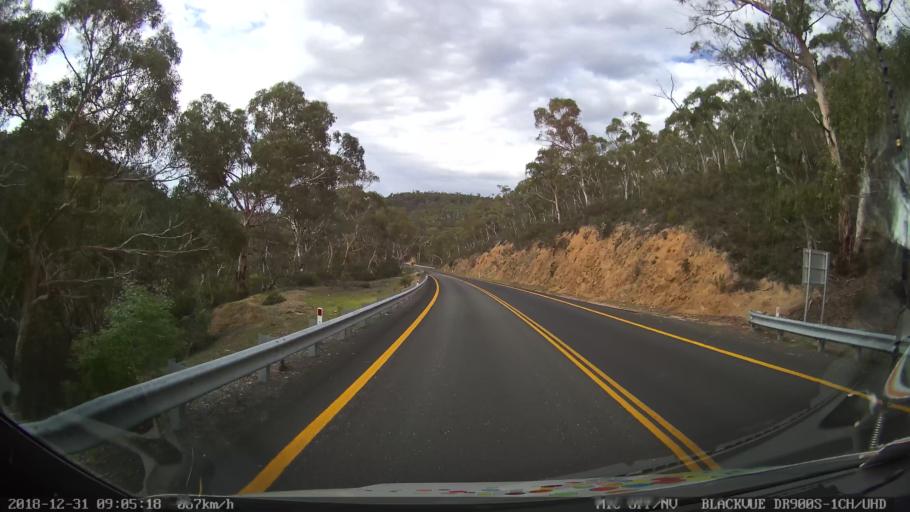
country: AU
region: New South Wales
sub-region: Snowy River
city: Jindabyne
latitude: -36.3619
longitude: 148.5872
